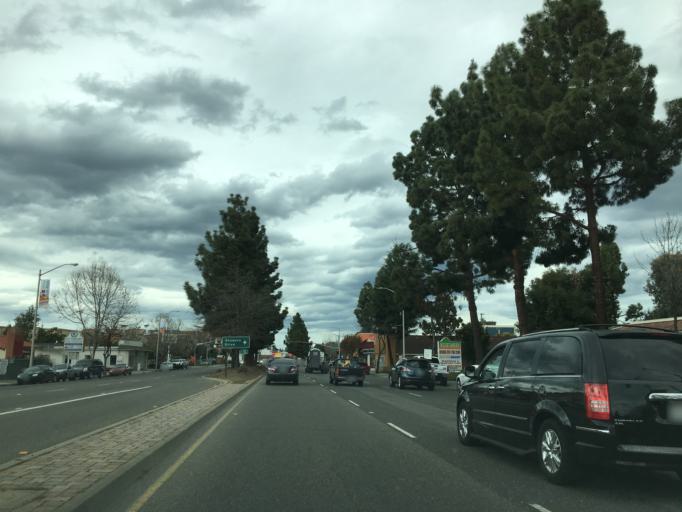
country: US
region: California
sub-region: Santa Clara County
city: Los Altos
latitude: 37.3986
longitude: -122.1082
